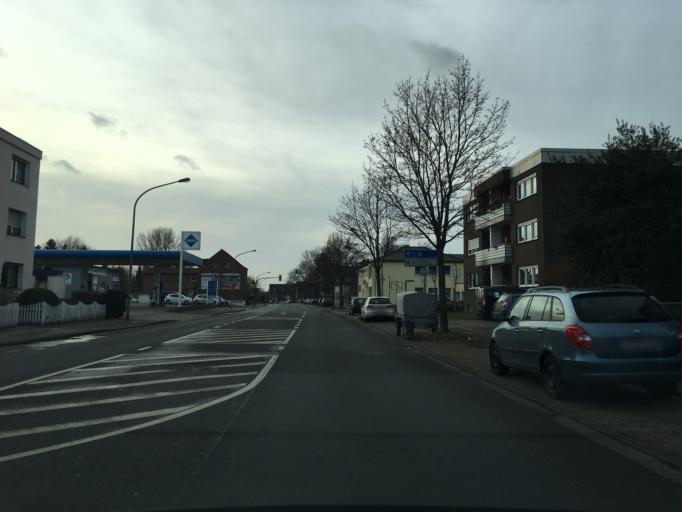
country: DE
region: North Rhine-Westphalia
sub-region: Regierungsbezirk Dusseldorf
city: Dinslaken
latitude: 51.5300
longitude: 6.7987
